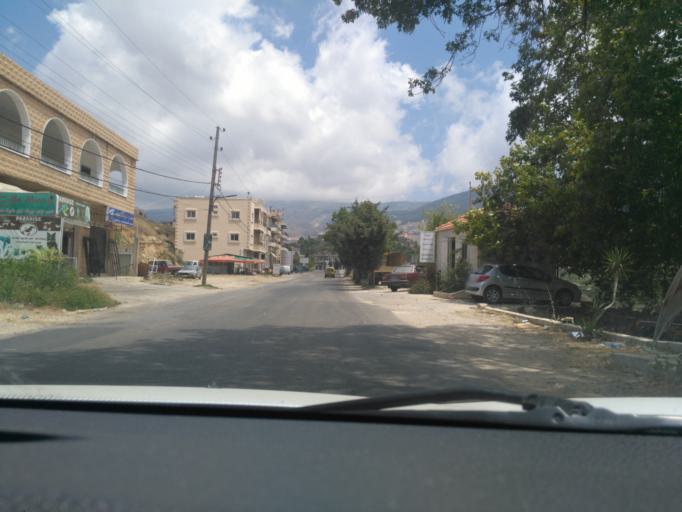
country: LB
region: Mont-Liban
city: Beit ed Dine
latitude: 33.7046
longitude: 35.6675
